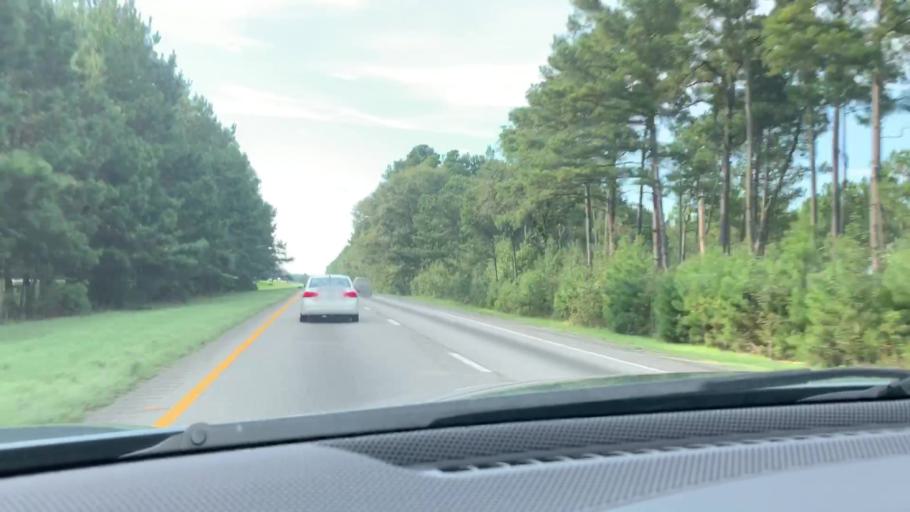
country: US
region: South Carolina
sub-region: Orangeburg County
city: Brookdale
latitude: 33.4383
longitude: -80.7031
